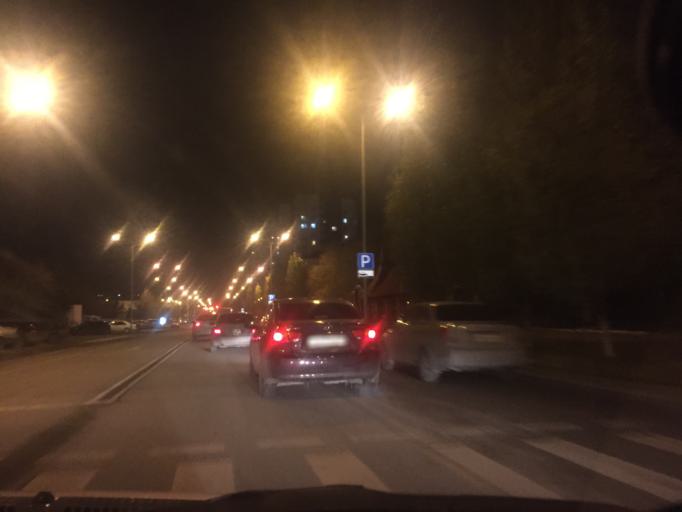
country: KZ
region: Astana Qalasy
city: Astana
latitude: 51.1856
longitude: 71.4131
